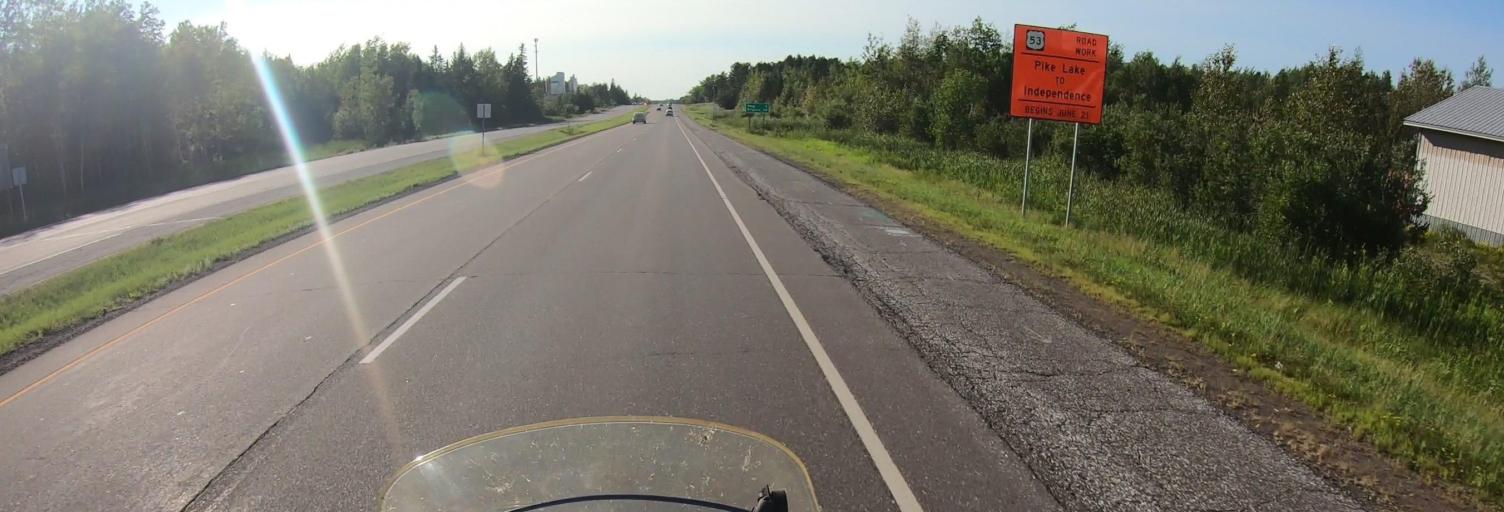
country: US
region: Minnesota
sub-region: Saint Louis County
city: Hermantown
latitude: 46.8449
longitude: -92.2600
